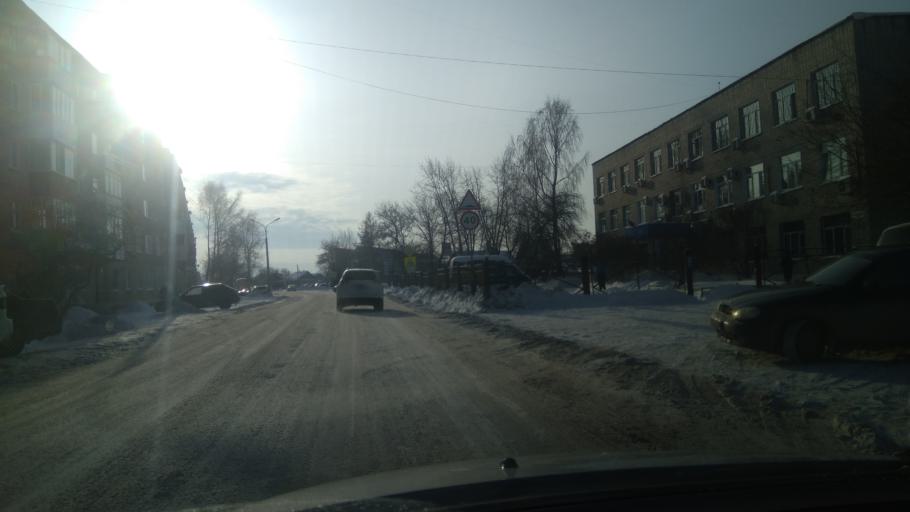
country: RU
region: Sverdlovsk
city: Sukhoy Log
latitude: 56.8982
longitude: 62.0314
